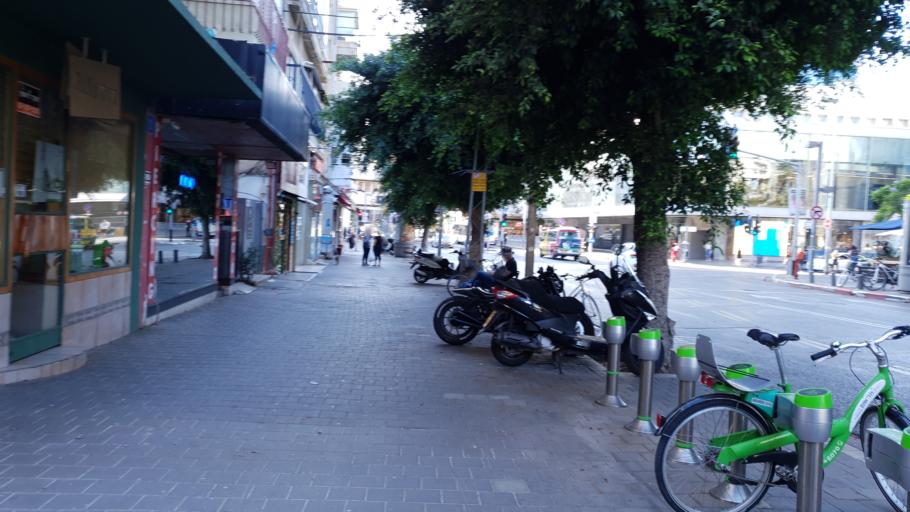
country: IL
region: Tel Aviv
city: Tel Aviv
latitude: 32.0765
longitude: 34.7747
